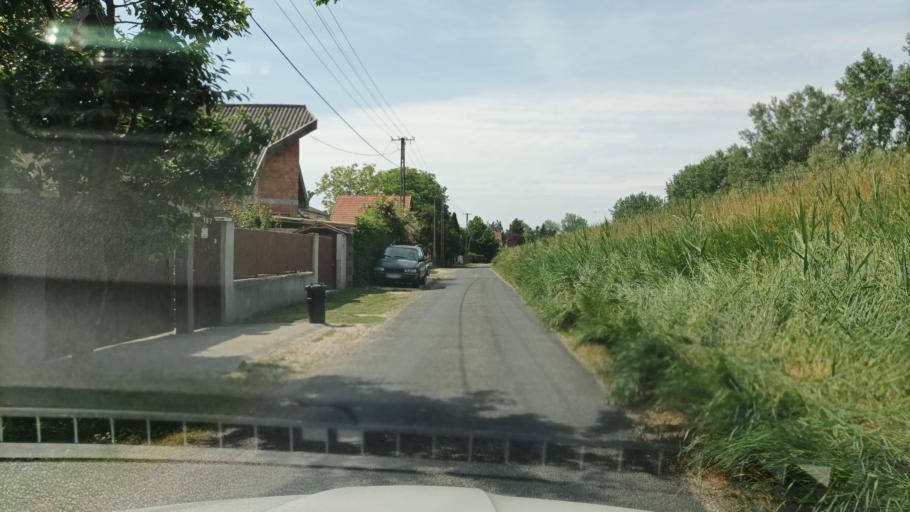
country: HU
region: Pest
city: Domsod
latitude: 47.0913
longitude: 18.9918
